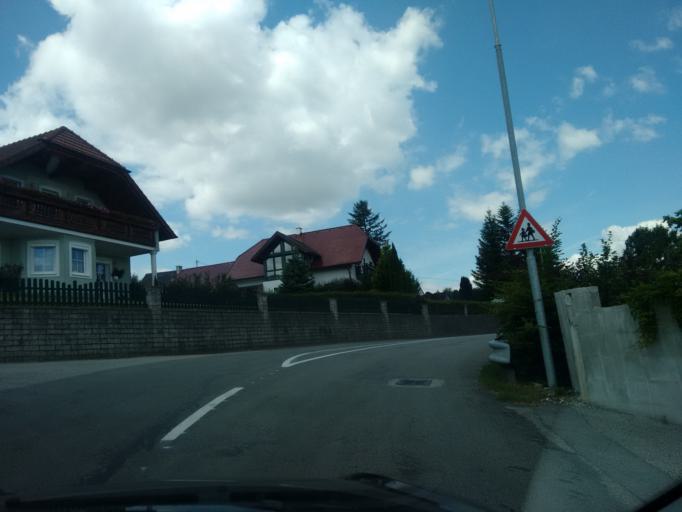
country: AT
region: Upper Austria
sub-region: Politischer Bezirk Steyr-Land
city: Sierning
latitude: 48.0395
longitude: 14.3077
